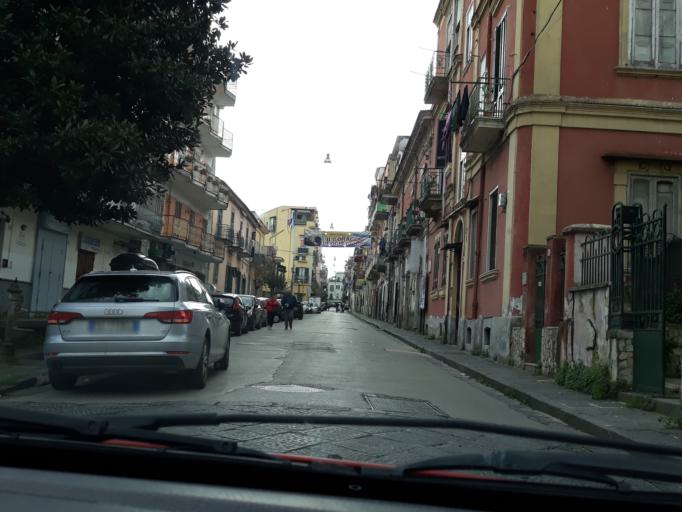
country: IT
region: Campania
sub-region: Provincia di Napoli
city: Mugnano di Napoli
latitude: 40.8890
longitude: 14.2306
